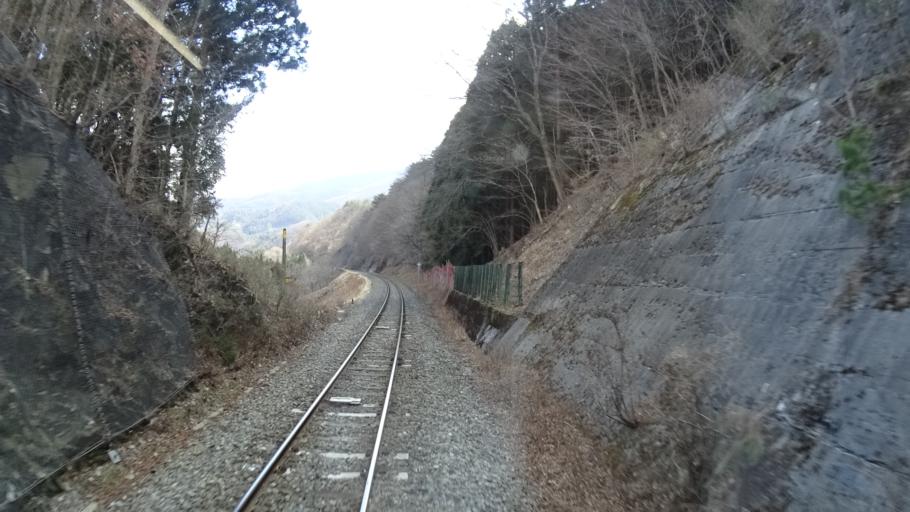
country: JP
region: Iwate
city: Kamaishi
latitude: 39.2592
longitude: 141.7310
